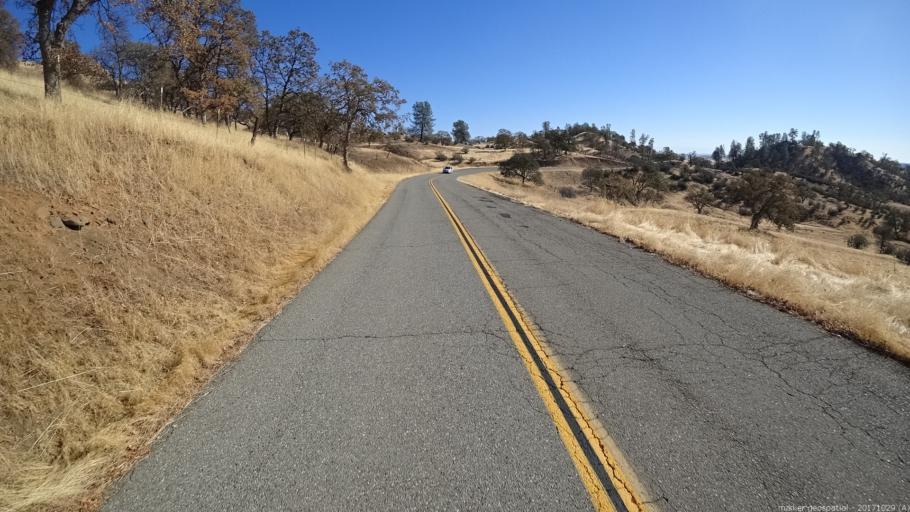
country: US
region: California
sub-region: Shasta County
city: Shasta
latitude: 40.4464
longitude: -122.6854
